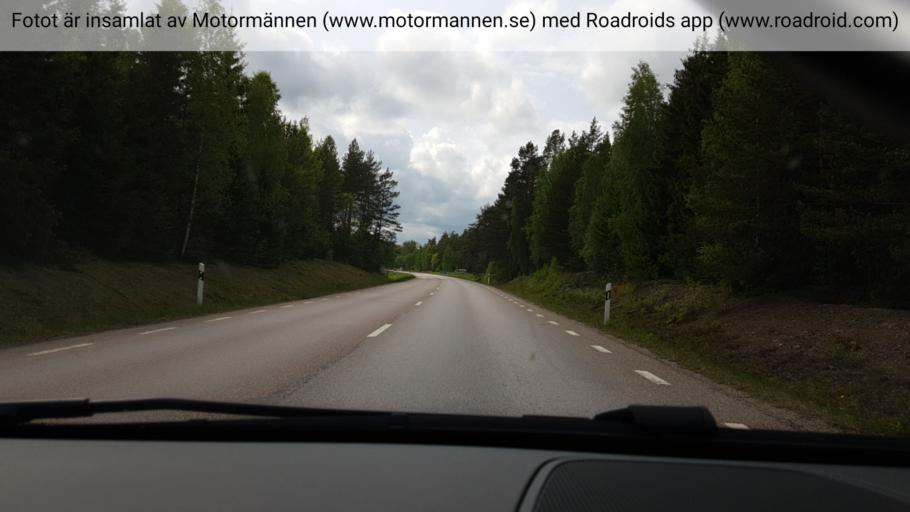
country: SE
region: Uppsala
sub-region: Tierps Kommun
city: Orbyhus
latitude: 60.2163
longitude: 17.7430
